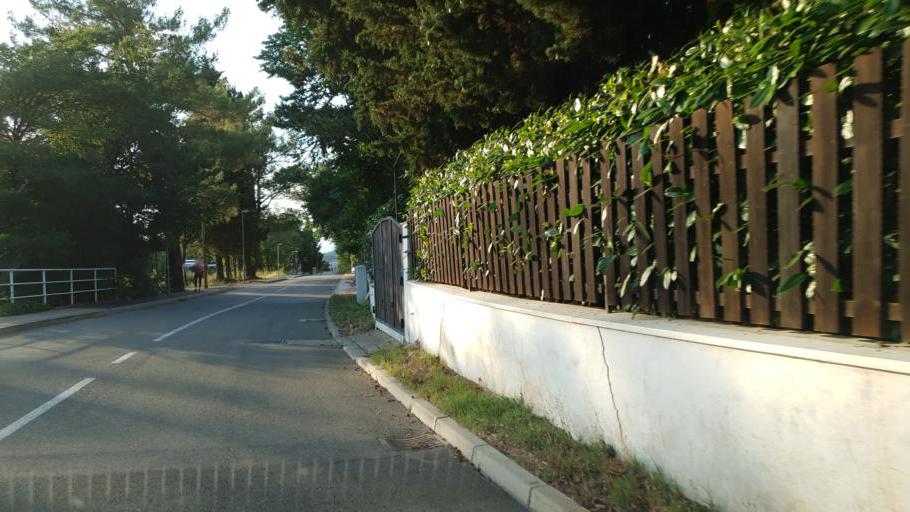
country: HR
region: Primorsko-Goranska
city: Omisalj
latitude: 45.2150
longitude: 14.5541
